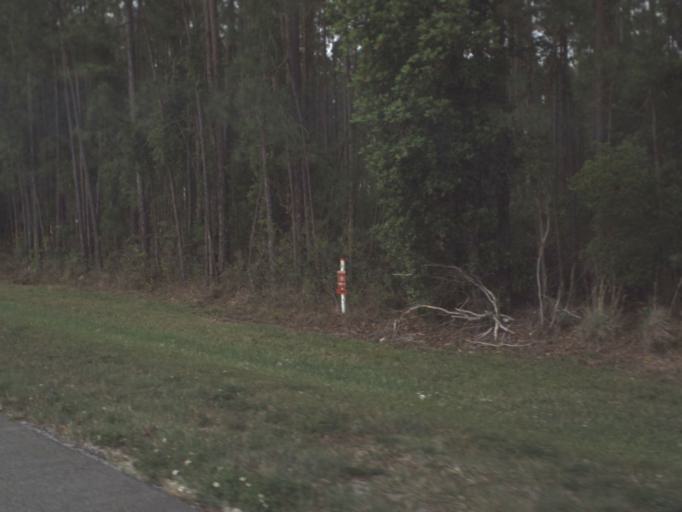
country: US
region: Florida
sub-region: Putnam County
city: Crescent City
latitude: 29.5226
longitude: -81.5079
